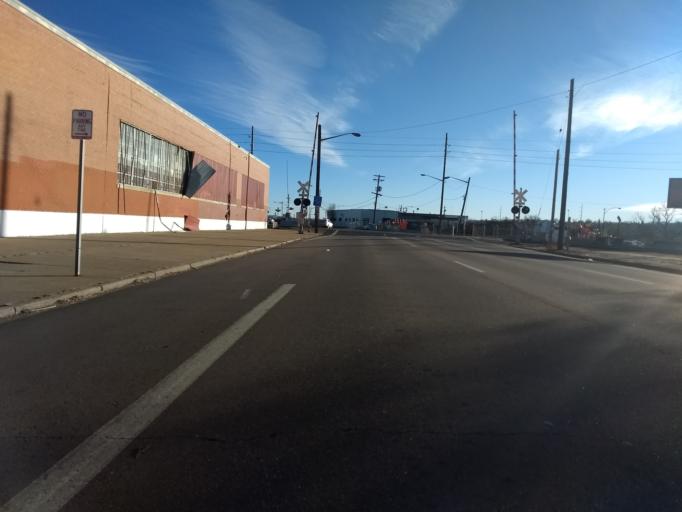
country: US
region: Colorado
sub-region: Denver County
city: Denver
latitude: 39.7156
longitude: -105.0001
